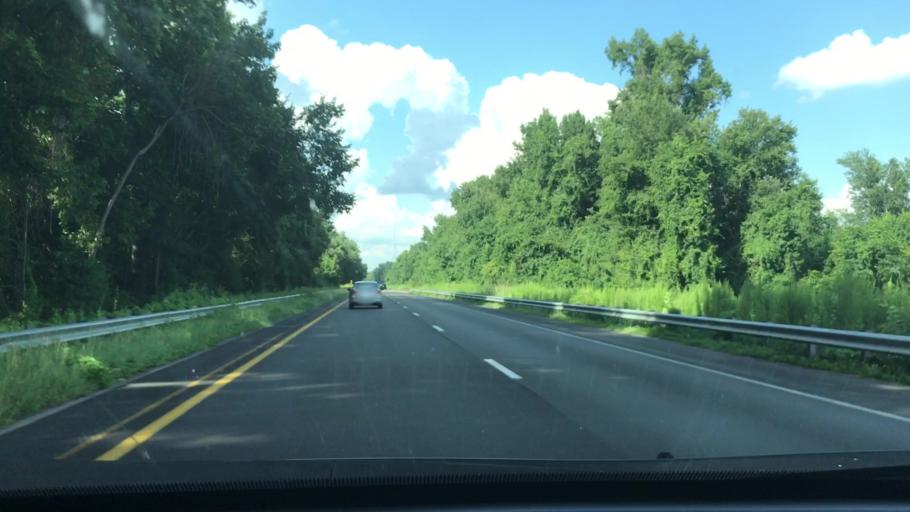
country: US
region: South Carolina
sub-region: Clarendon County
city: Manning
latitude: 33.8367
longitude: -80.1282
